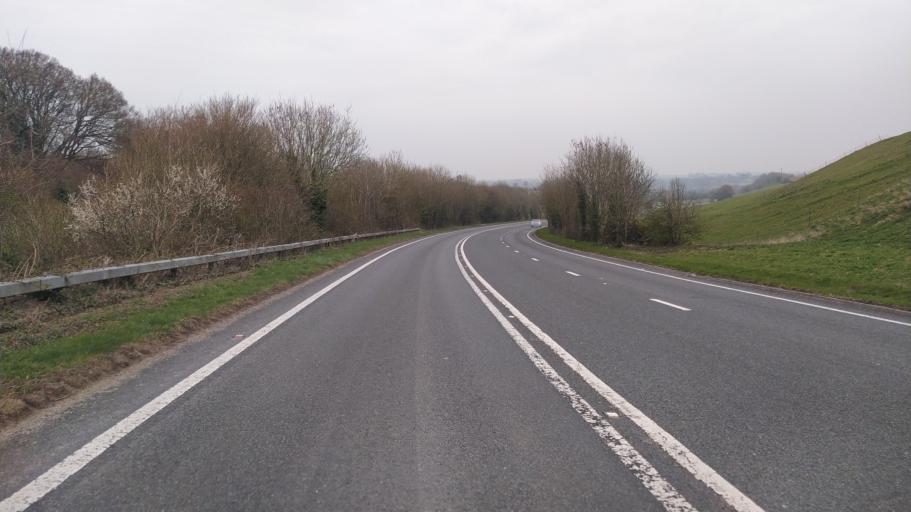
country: GB
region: England
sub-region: Dorset
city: Dorchester
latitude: 50.7169
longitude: -2.4731
